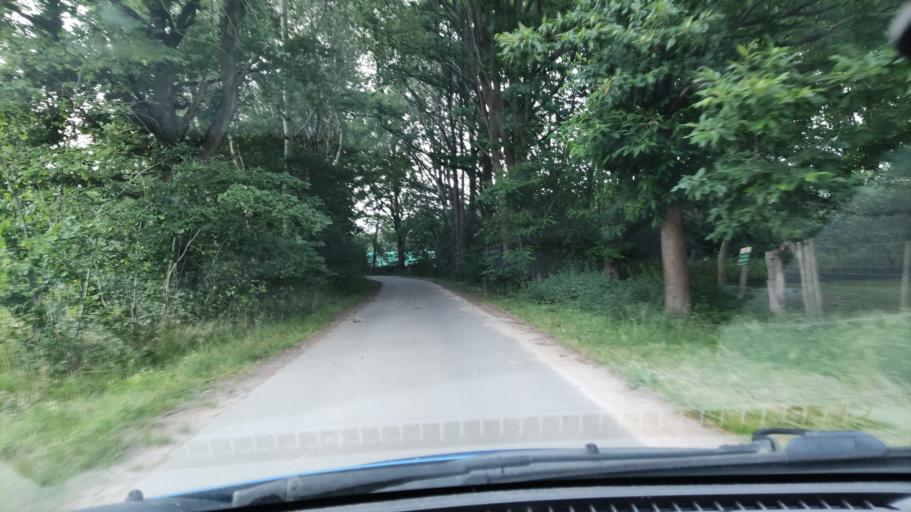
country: DE
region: Lower Saxony
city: Amelinghausen
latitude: 53.1312
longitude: 10.2484
